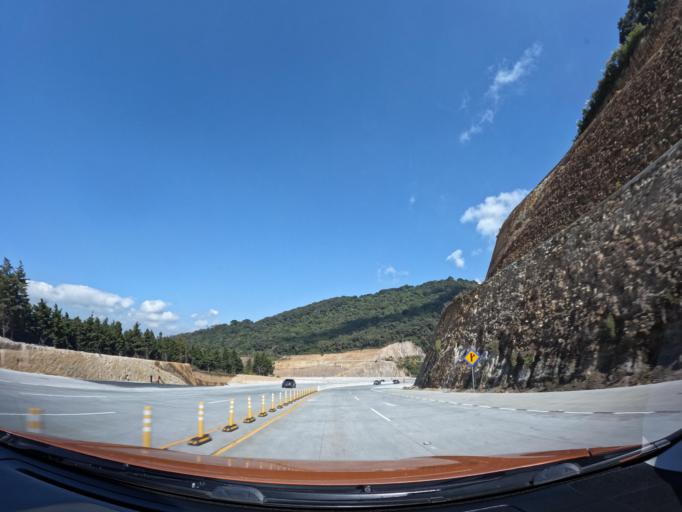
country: GT
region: Guatemala
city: Villa Canales
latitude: 14.4920
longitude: -90.4993
